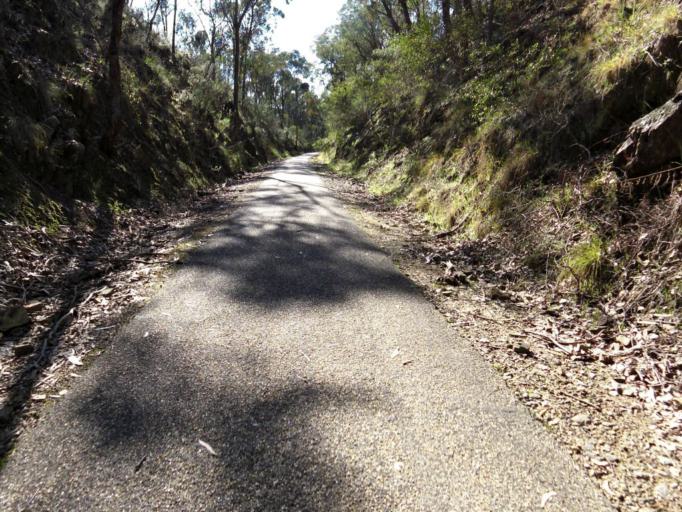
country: AU
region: Victoria
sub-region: Wangaratta
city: Wangaratta
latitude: -36.4082
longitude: 146.6169
